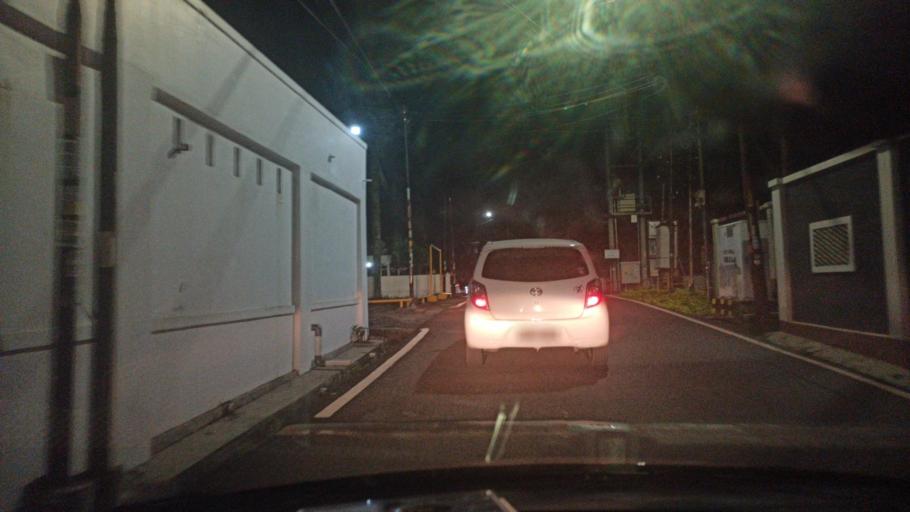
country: ID
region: South Sumatra
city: Plaju
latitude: -3.0024
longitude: 104.7246
